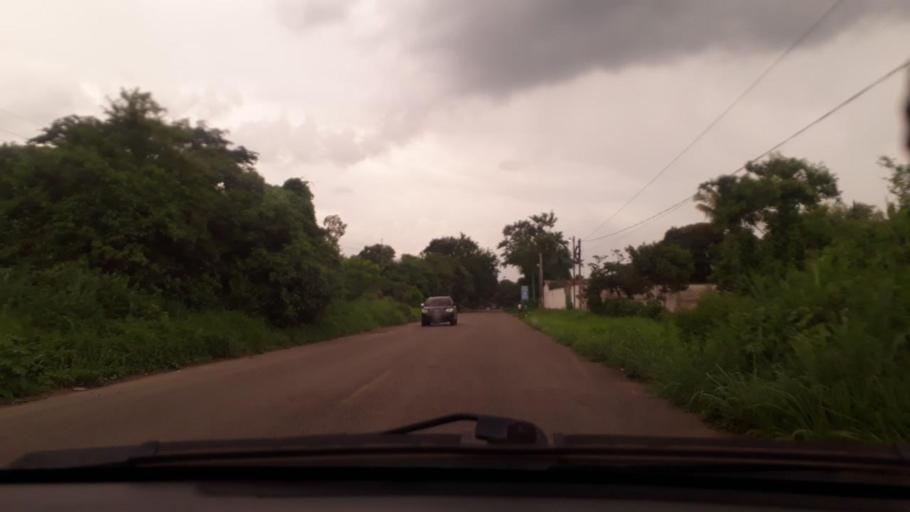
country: GT
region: Jutiapa
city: Jalpatagua
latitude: 14.1545
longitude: -90.0470
